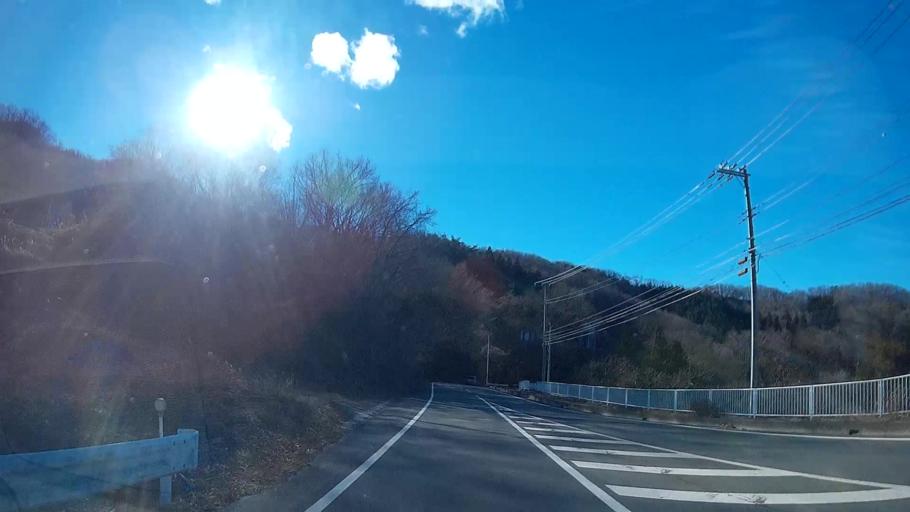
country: JP
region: Saitama
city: Yorii
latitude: 36.0749
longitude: 139.1143
